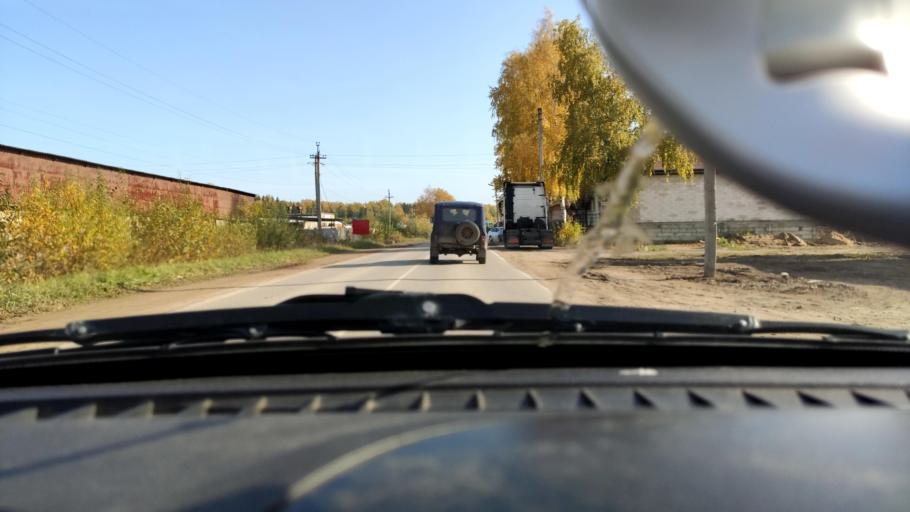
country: RU
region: Perm
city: Overyata
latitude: 58.0573
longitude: 55.8856
